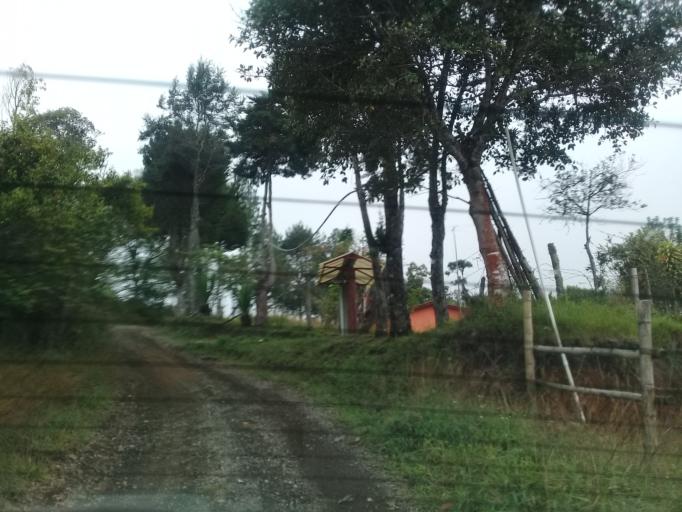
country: CO
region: Cundinamarca
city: Viani
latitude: 4.8371
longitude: -74.5531
